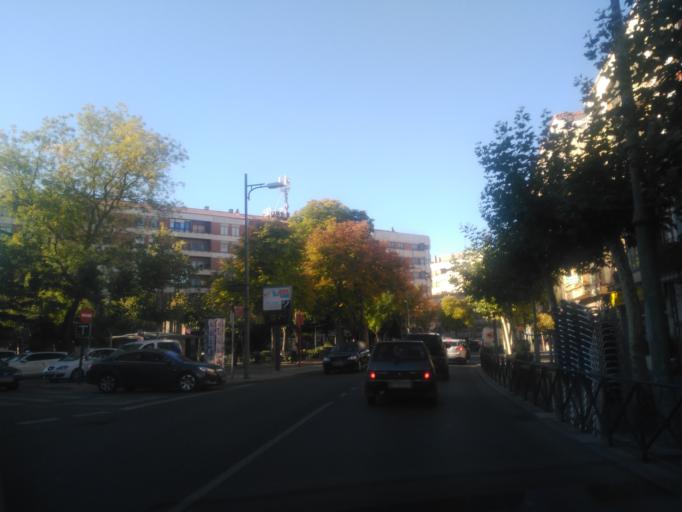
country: ES
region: Castille and Leon
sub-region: Provincia de Burgos
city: Aranda de Duero
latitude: 41.6707
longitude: -3.6853
